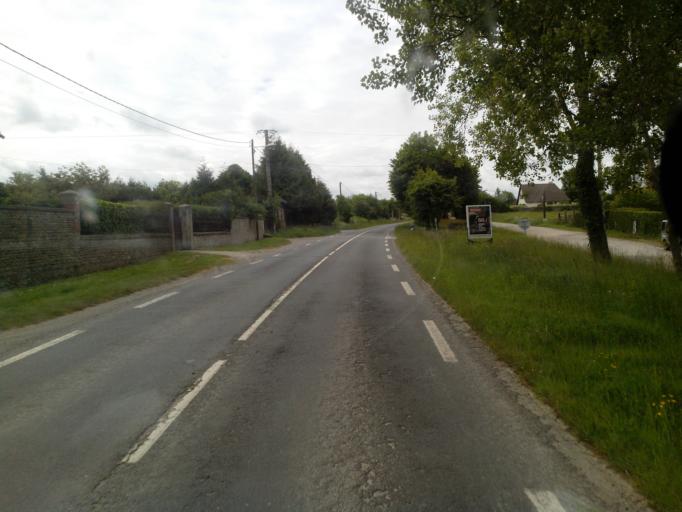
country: FR
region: Lower Normandy
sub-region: Departement du Calvados
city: Amfreville
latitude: 49.2500
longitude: -0.2447
